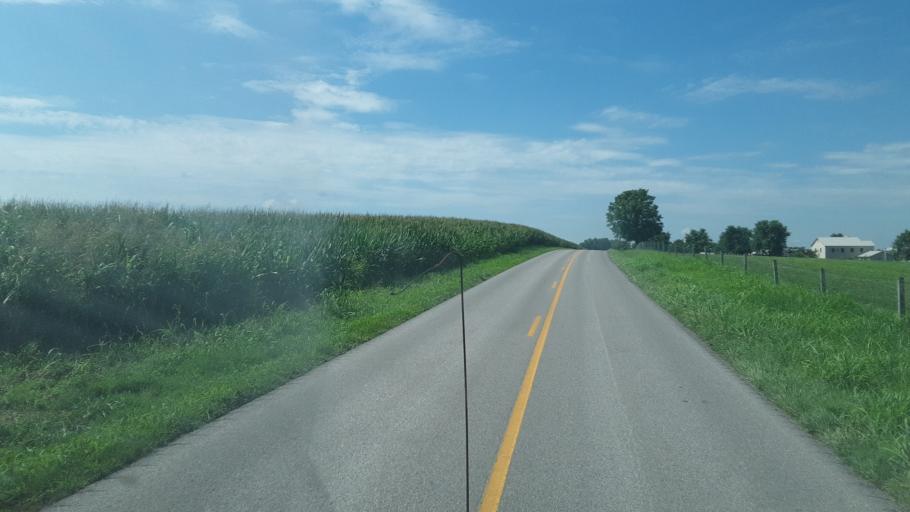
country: US
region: Kentucky
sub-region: Todd County
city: Elkton
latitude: 36.8062
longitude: -87.3158
